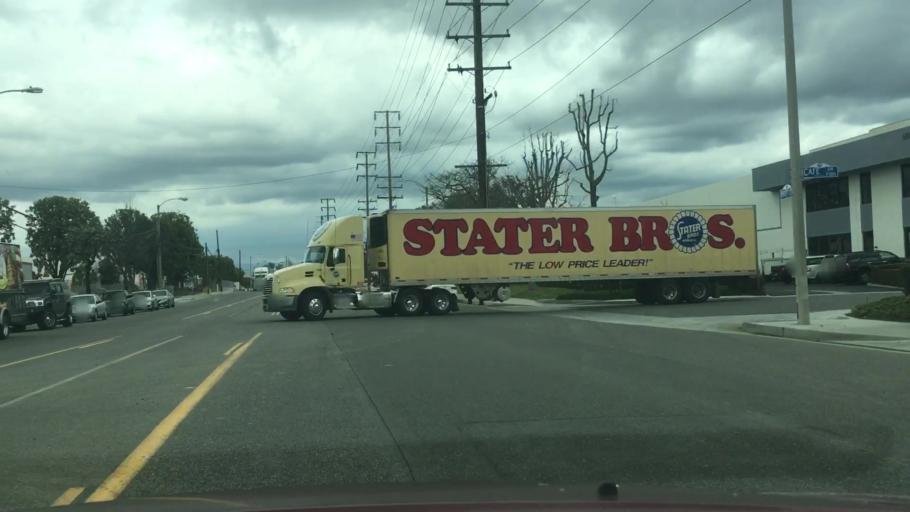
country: US
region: California
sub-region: Orange County
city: Buena Park
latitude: 33.8764
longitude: -118.0114
